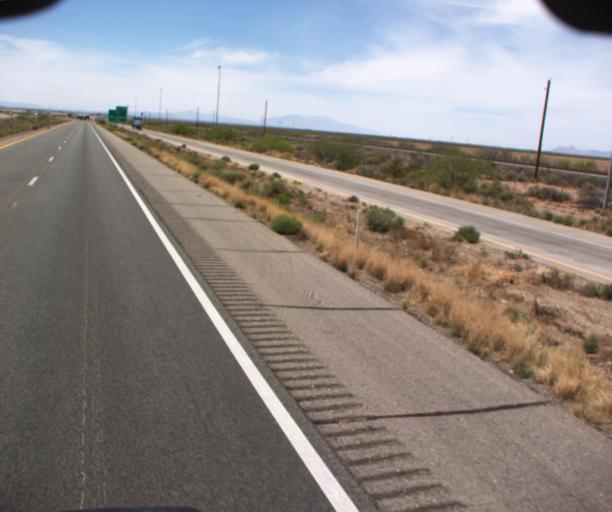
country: US
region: New Mexico
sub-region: Hidalgo County
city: Lordsburg
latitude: 32.2561
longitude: -109.1720
